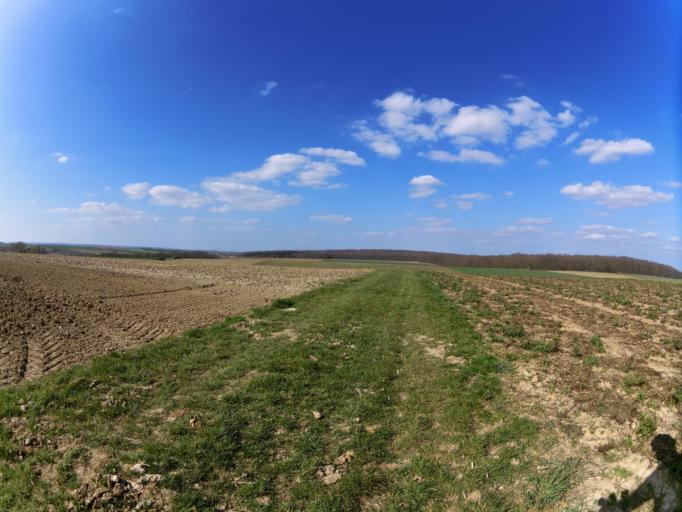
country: DE
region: Bavaria
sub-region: Regierungsbezirk Unterfranken
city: Nordheim
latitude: 49.8367
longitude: 10.1609
